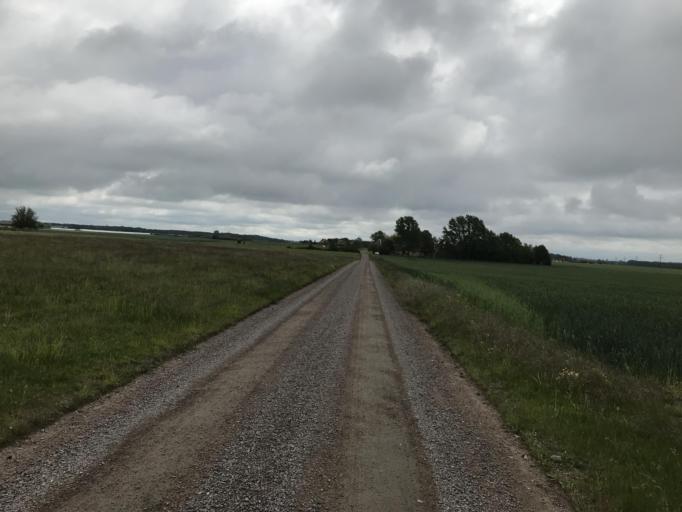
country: SE
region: Skane
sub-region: Landskrona
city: Asmundtorp
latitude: 55.8699
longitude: 12.9102
